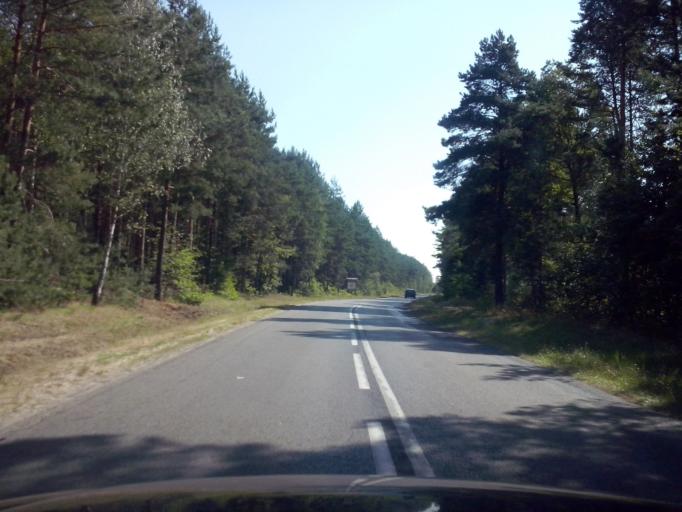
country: PL
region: Swietokrzyskie
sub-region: Powiat kielecki
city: Domaszowice
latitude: 50.8142
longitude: 20.7161
